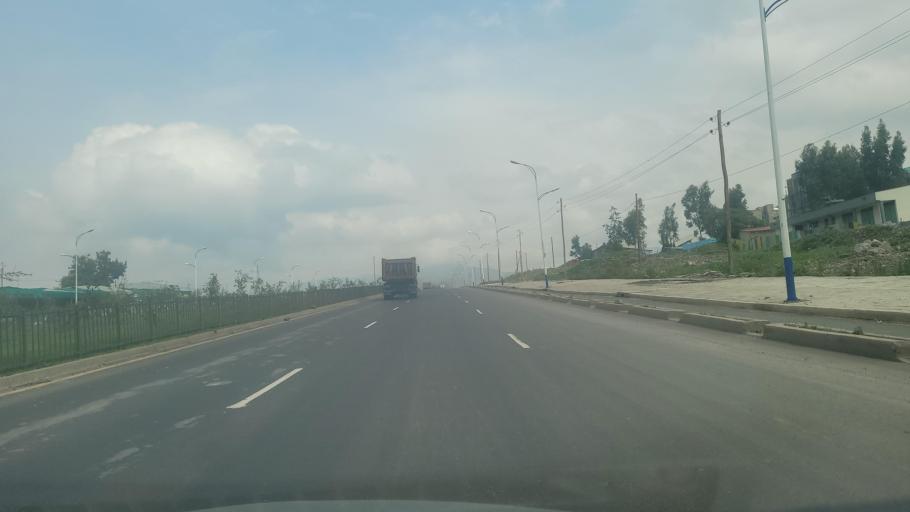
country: ET
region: Adis Abeba
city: Addis Ababa
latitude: 8.9495
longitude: 38.7079
